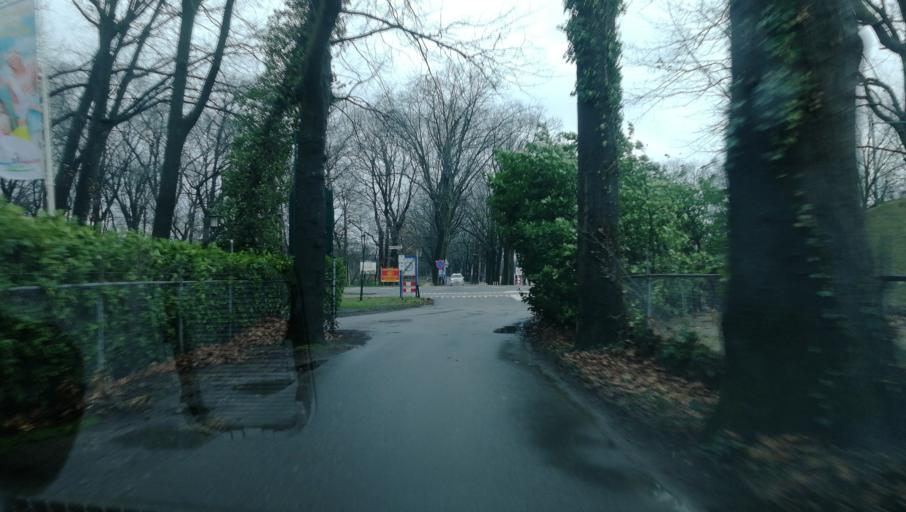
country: NL
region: Limburg
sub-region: Gemeente Venlo
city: Tegelen
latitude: 51.3448
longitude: 6.1053
